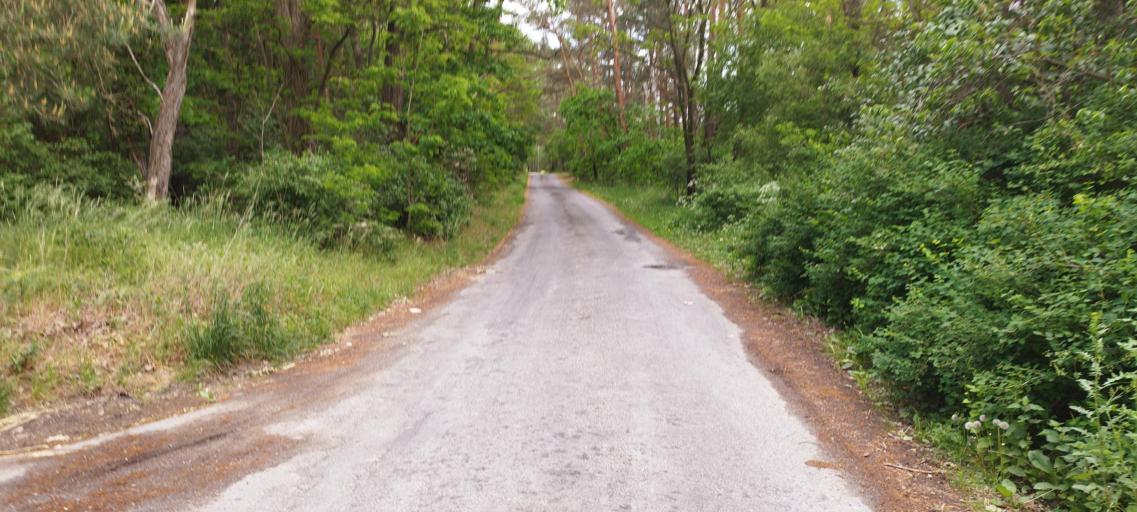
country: DE
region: Brandenburg
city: Berkenbruck
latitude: 52.3585
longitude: 14.1561
